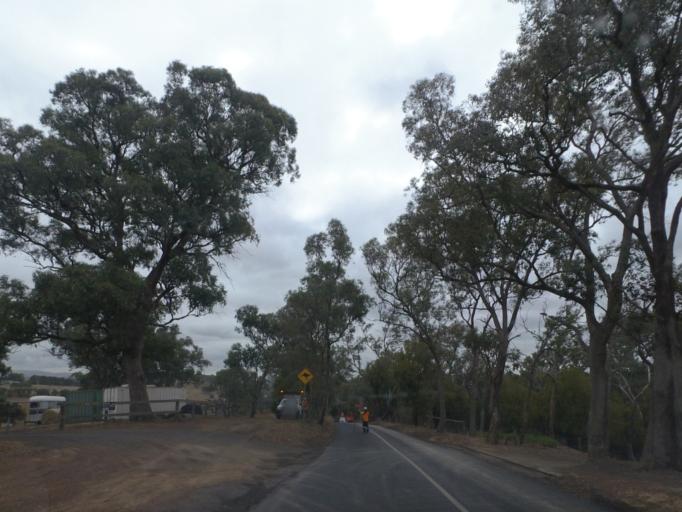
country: AU
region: Victoria
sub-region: Nillumbik
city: North Warrandyte
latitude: -37.6960
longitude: 145.2389
